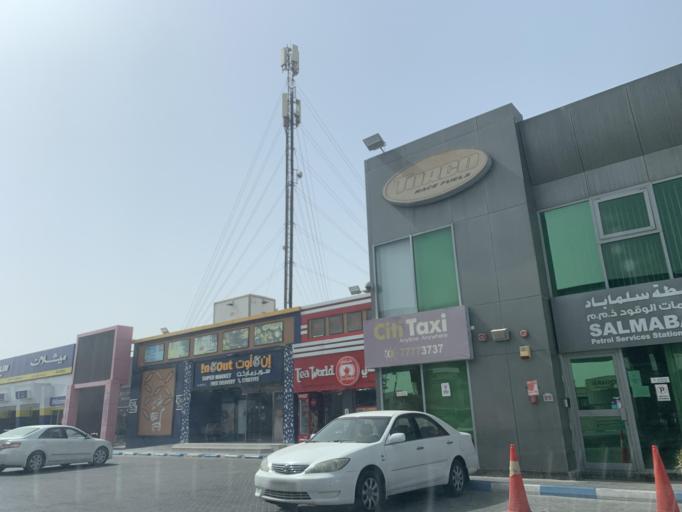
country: BH
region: Northern
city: Madinat `Isa
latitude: 26.1872
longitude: 50.5185
